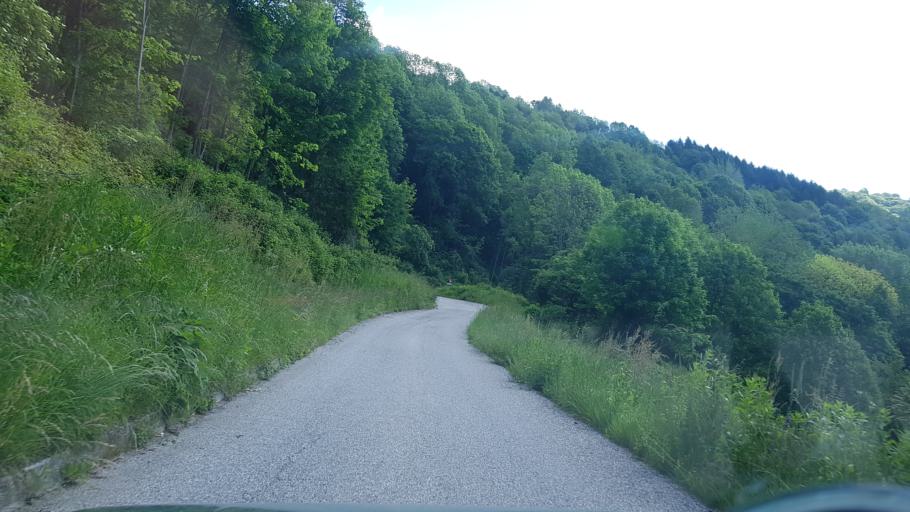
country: IT
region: Friuli Venezia Giulia
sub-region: Provincia di Udine
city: Torreano
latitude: 46.1752
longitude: 13.4335
